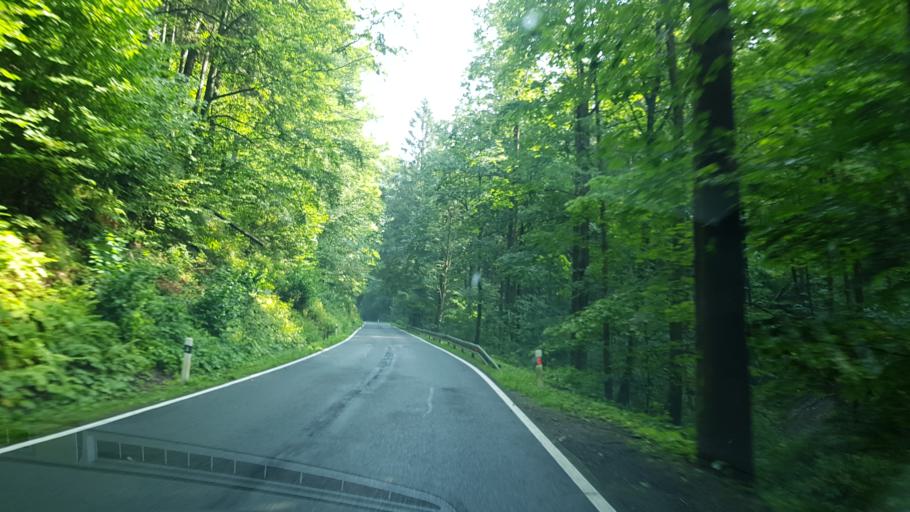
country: CZ
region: Olomoucky
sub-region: Okres Jesenik
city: Jesenik
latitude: 50.2062
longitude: 17.2429
